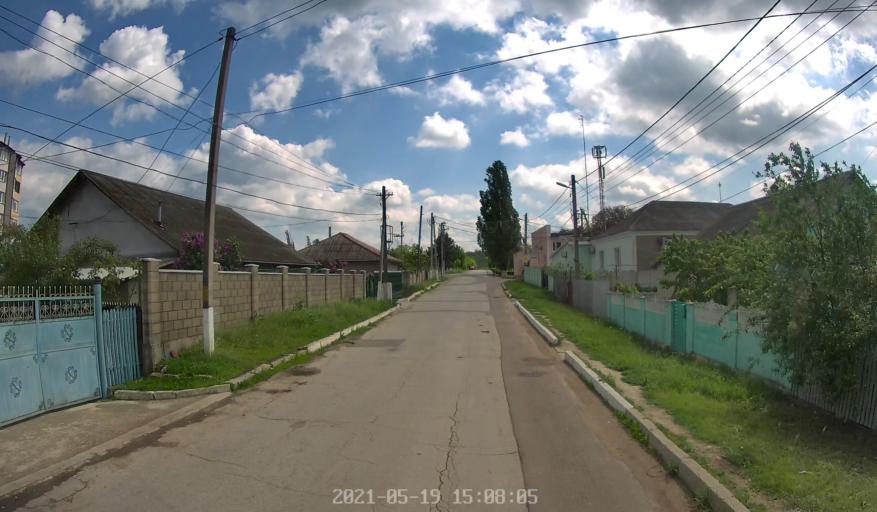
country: MD
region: Chisinau
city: Stauceni
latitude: 47.0619
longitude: 28.9483
